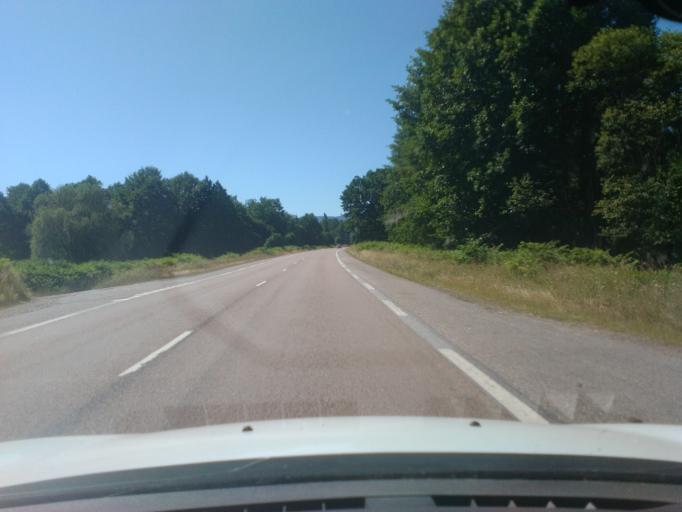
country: FR
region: Lorraine
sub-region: Departement des Vosges
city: Vagney
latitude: 48.0149
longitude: 6.7087
